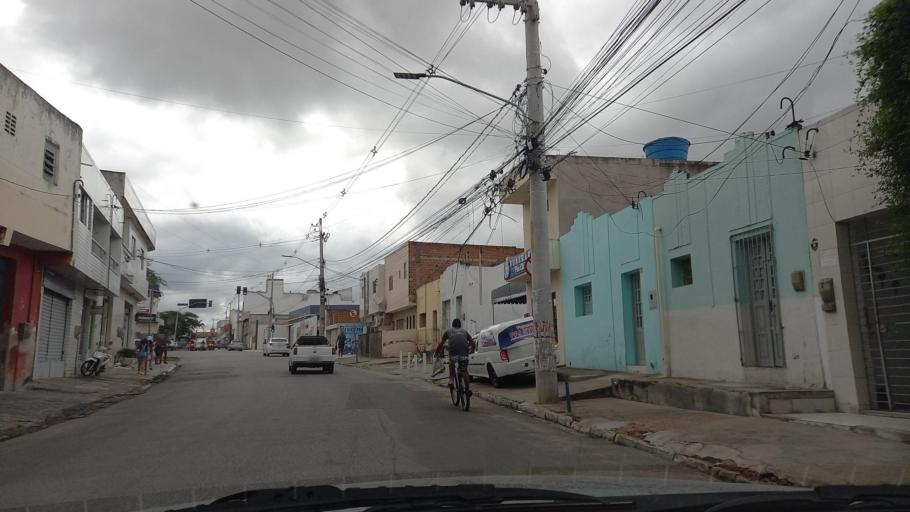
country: BR
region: Pernambuco
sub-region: Caruaru
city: Caruaru
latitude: -8.2739
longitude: -35.9643
